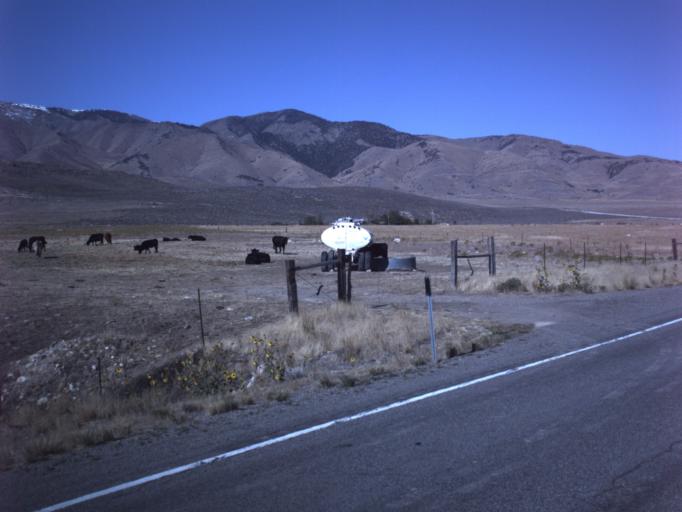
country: US
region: Utah
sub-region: Tooele County
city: Grantsville
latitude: 40.6337
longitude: -112.5166
